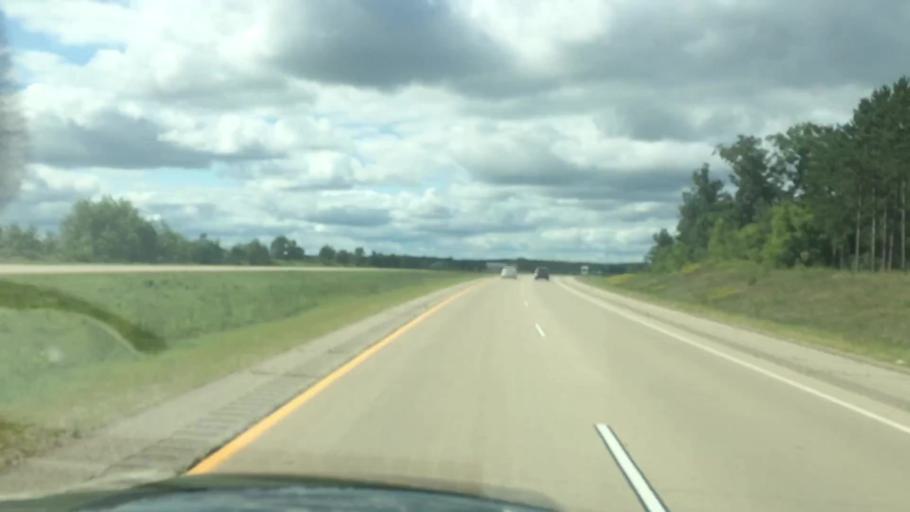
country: US
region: Wisconsin
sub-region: Portage County
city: Amherst
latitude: 44.5028
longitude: -89.4050
